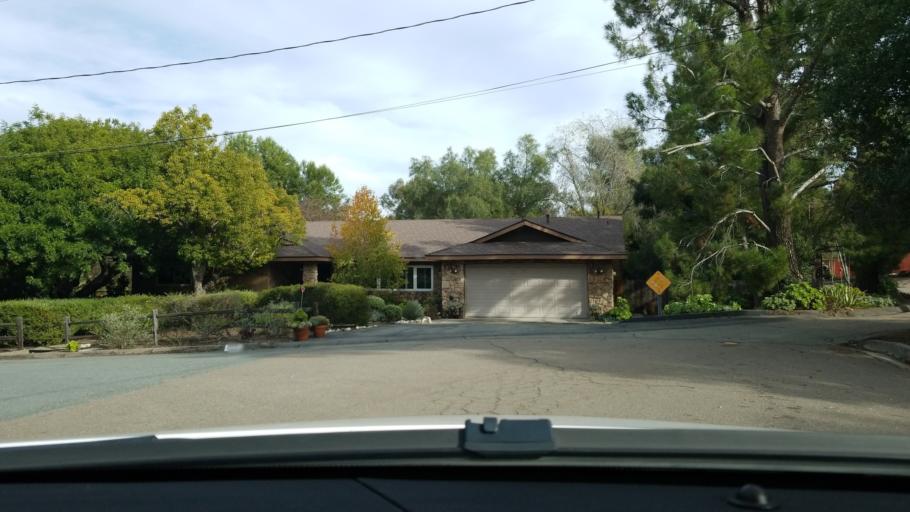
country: US
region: California
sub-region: San Diego County
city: Casa de Oro-Mount Helix
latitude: 32.7716
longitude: -116.9452
